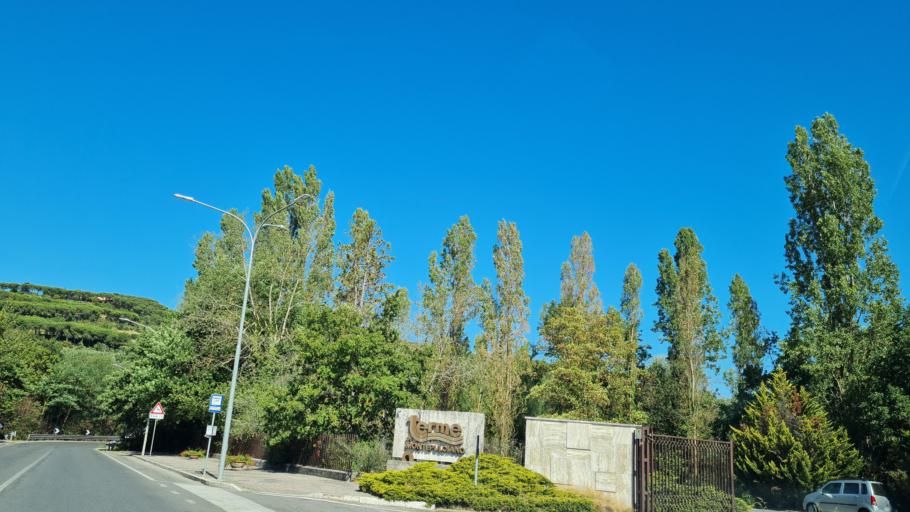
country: IT
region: Tuscany
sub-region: Provincia di Siena
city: Sant'Albino
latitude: 43.0729
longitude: 11.8015
